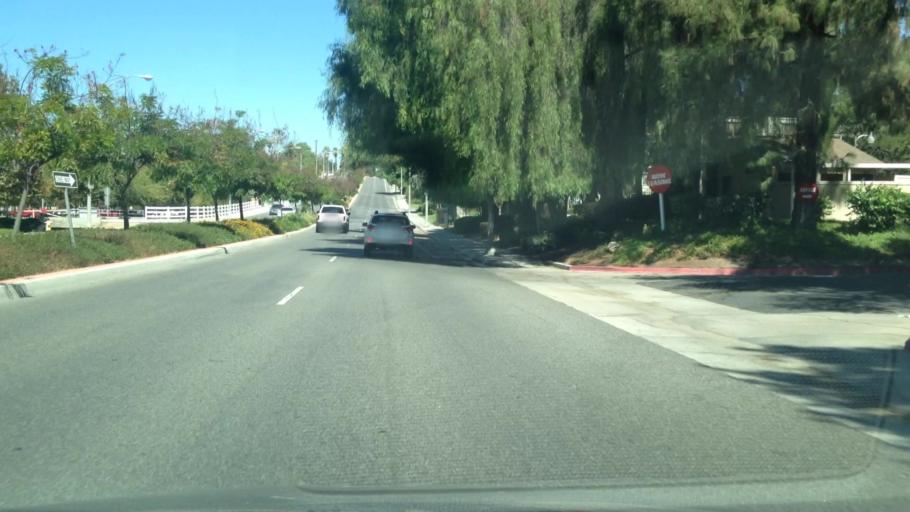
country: US
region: California
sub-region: Riverside County
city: Riverside
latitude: 33.9573
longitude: -117.3468
